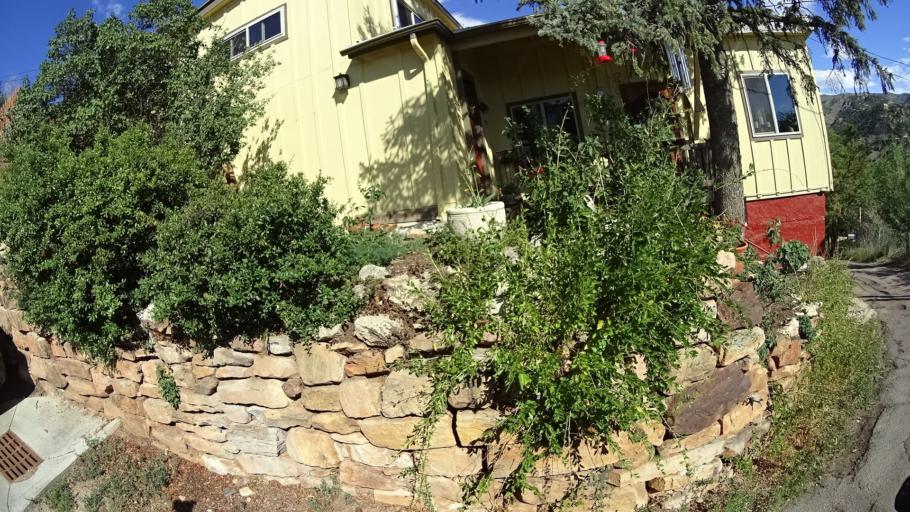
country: US
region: Colorado
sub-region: El Paso County
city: Manitou Springs
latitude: 38.8561
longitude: -104.9197
